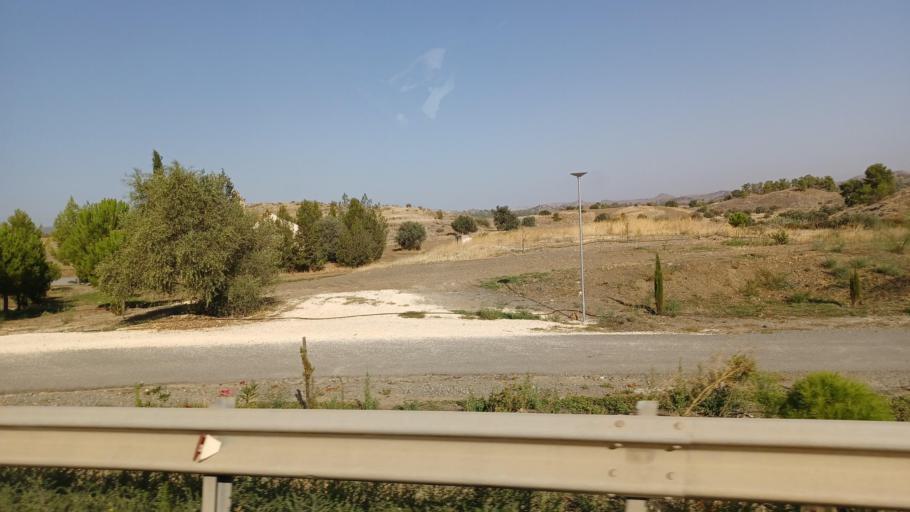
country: CY
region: Lefkosia
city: Lythrodontas
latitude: 34.9661
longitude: 33.3381
